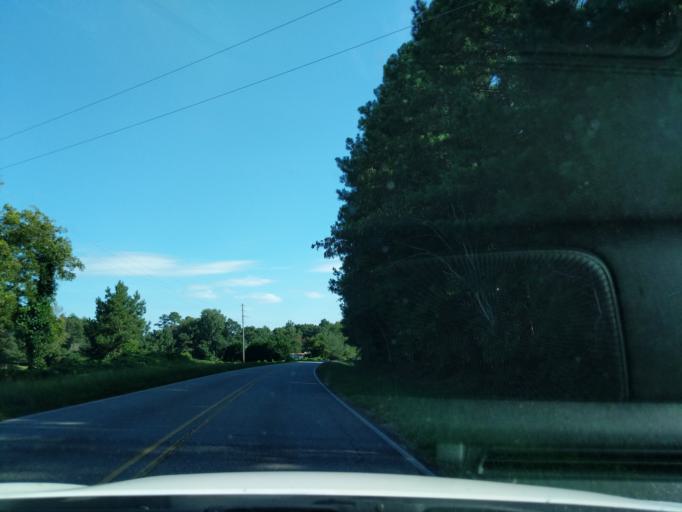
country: US
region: Georgia
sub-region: Oglethorpe County
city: Lexington
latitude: 33.8990
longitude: -82.9918
